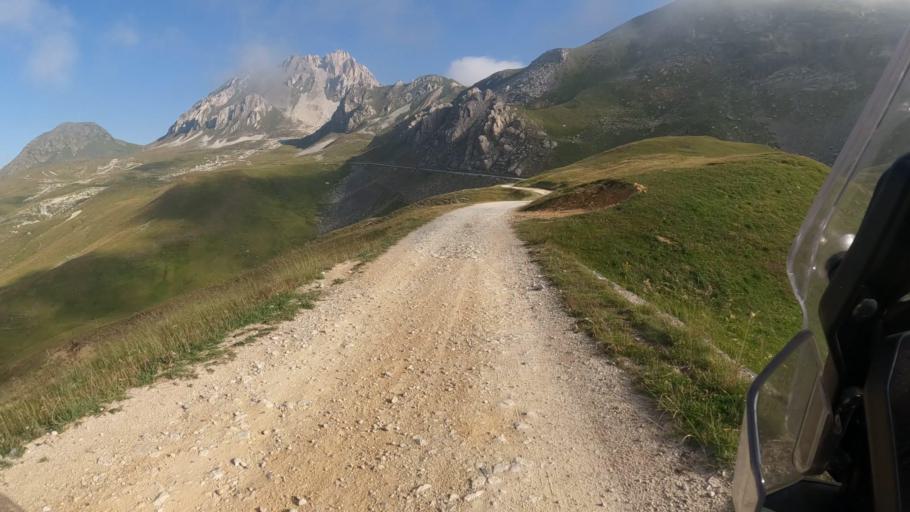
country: IT
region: Piedmont
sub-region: Provincia di Cuneo
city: Sambuco
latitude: 44.3818
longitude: 7.1001
